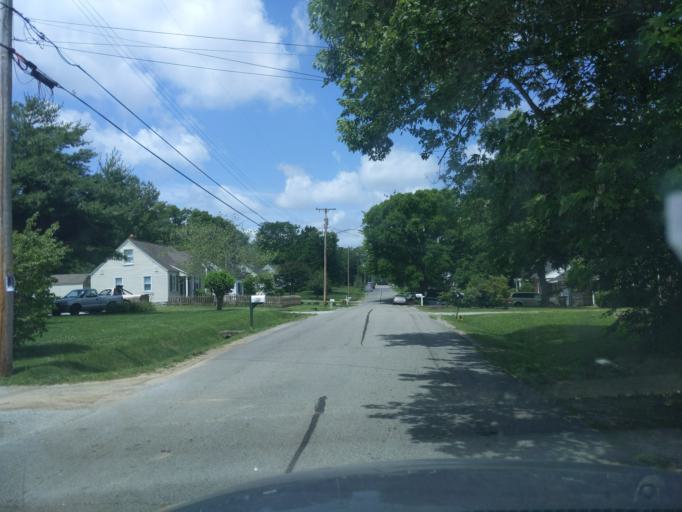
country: US
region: Tennessee
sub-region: Davidson County
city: Oak Hill
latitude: 36.1073
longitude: -86.7380
